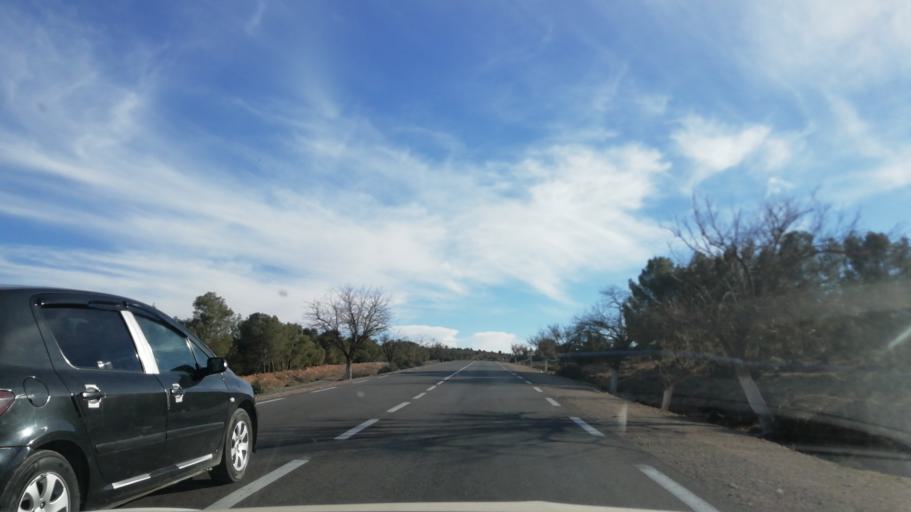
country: DZ
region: Tlemcen
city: Sebdou
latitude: 34.5890
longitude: -1.3180
